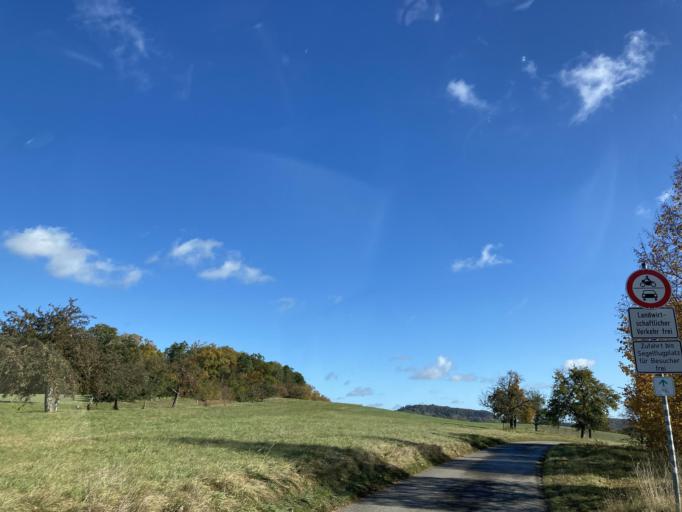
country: DE
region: Baden-Wuerttemberg
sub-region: Tuebingen Region
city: Rottenburg
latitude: 48.5512
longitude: 8.9390
